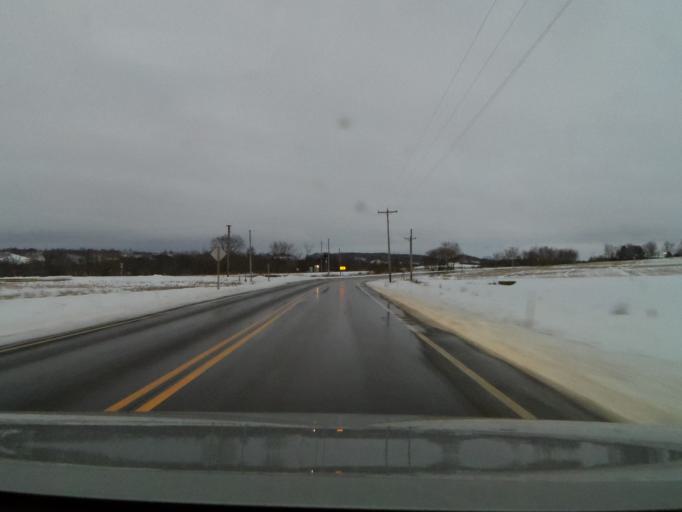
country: US
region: Wisconsin
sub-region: Dunn County
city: Boyceville
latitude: 44.9556
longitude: -92.0618
